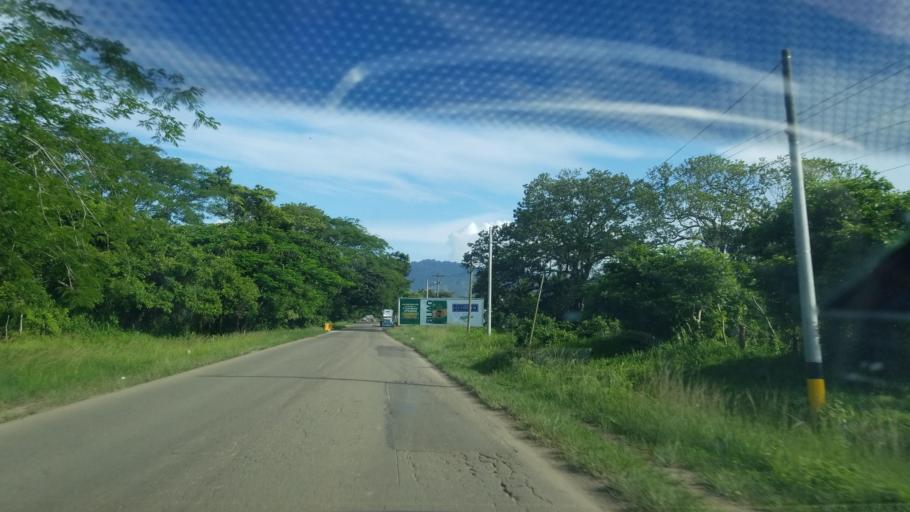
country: HN
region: El Paraiso
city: Cuyali
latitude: 13.8954
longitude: -86.5554
